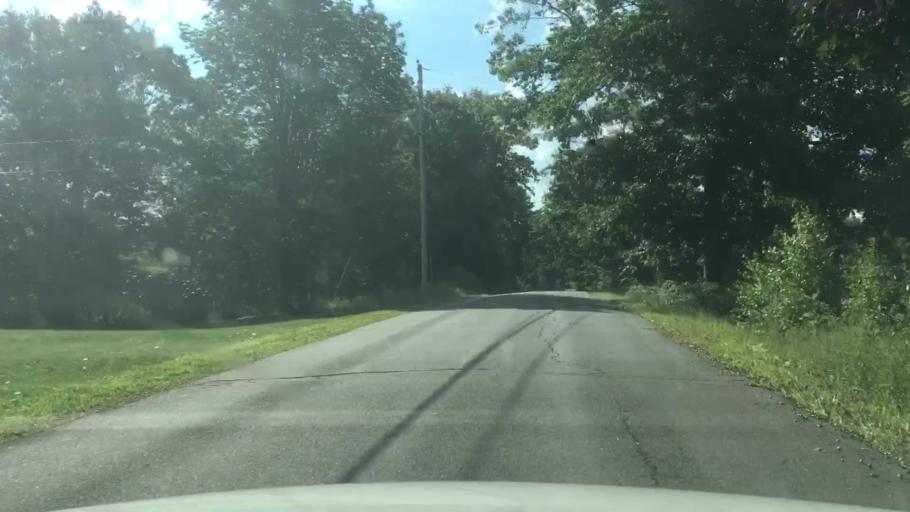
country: US
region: Maine
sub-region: Kennebec County
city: Gardiner
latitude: 44.1696
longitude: -69.8148
